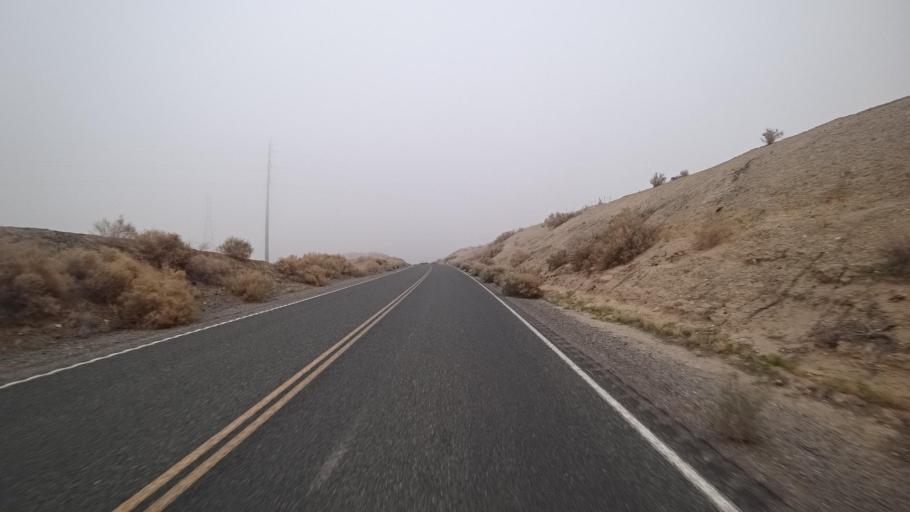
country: US
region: California
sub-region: Kern County
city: Buttonwillow
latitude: 35.3045
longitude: -119.4657
